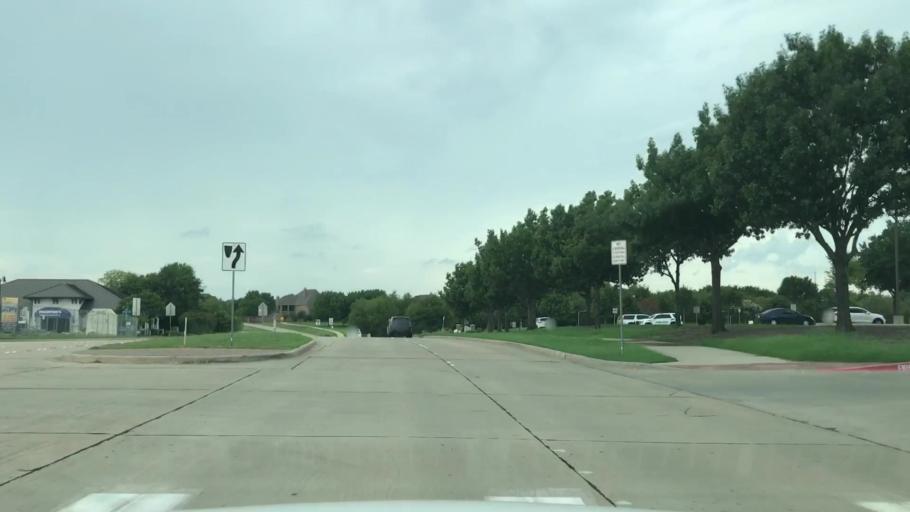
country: US
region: Texas
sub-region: Collin County
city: Frisco
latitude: 33.1297
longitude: -96.8104
